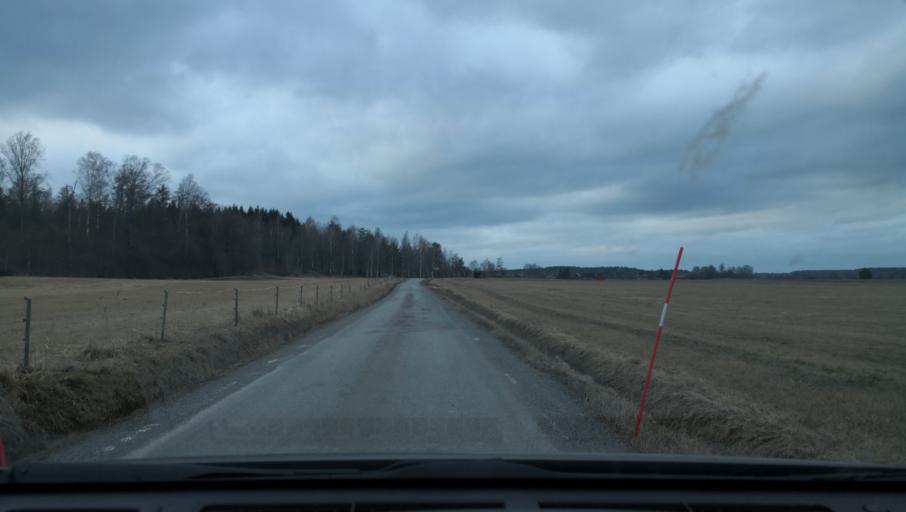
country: SE
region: Vaestmanland
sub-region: Kopings Kommun
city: Kolsva
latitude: 59.5562
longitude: 15.8724
